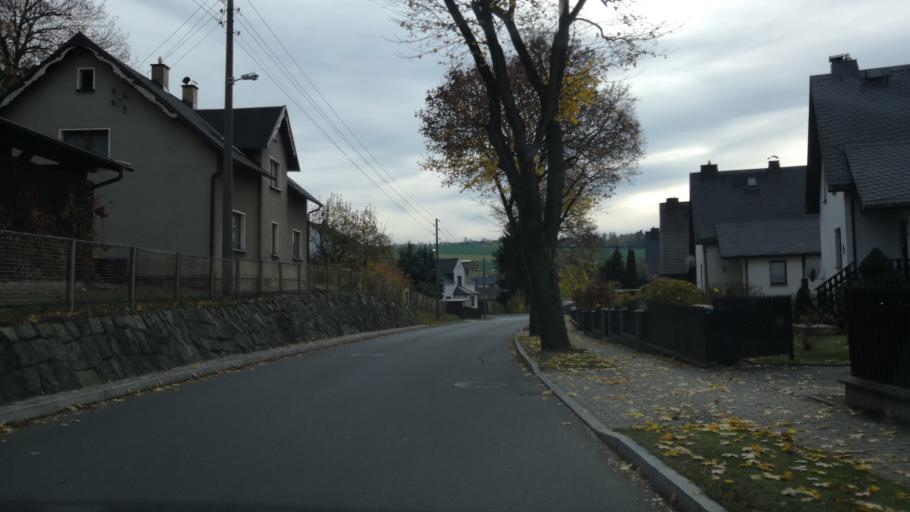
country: DE
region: Saxony
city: Rodewisch
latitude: 50.5340
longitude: 12.4199
